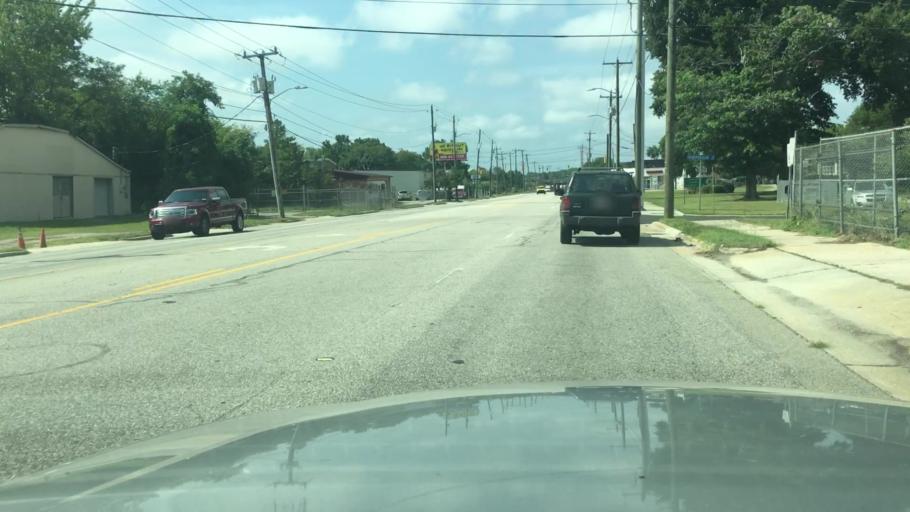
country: US
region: North Carolina
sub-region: Cumberland County
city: Fayetteville
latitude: 35.0434
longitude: -78.8816
